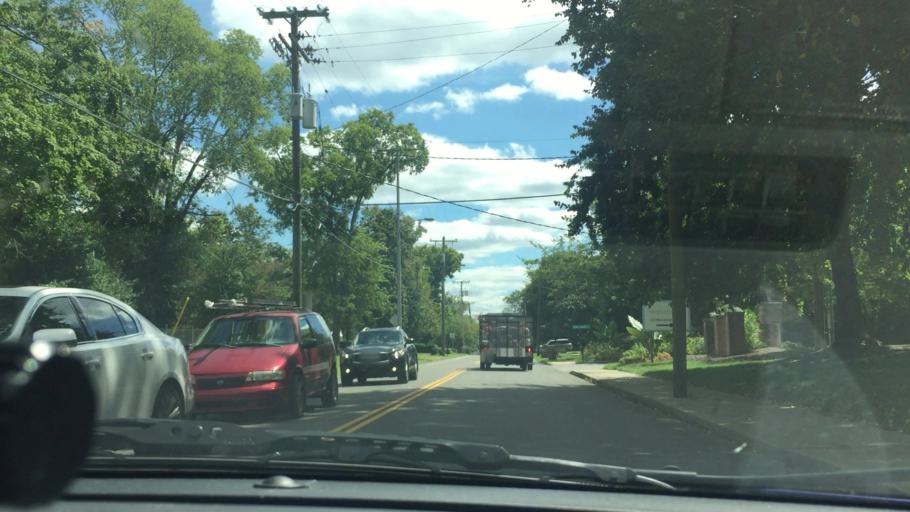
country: US
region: Tennessee
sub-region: Davidson County
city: Belle Meade
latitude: 36.1235
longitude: -86.8463
